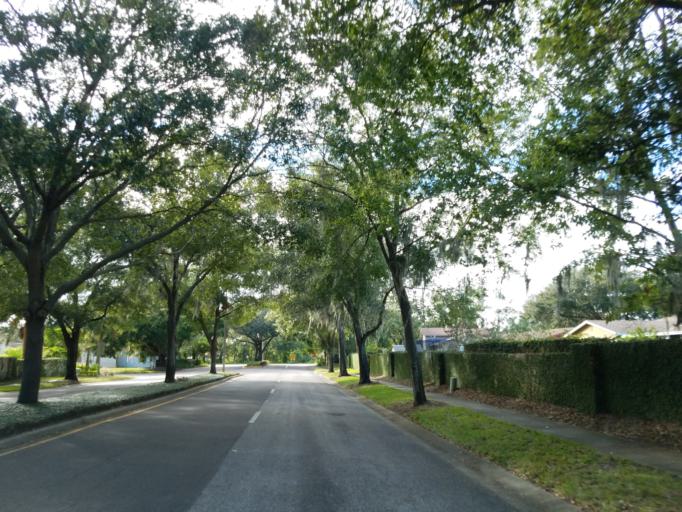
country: US
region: Florida
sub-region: Hillsborough County
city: Bloomingdale
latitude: 27.8852
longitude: -82.2679
